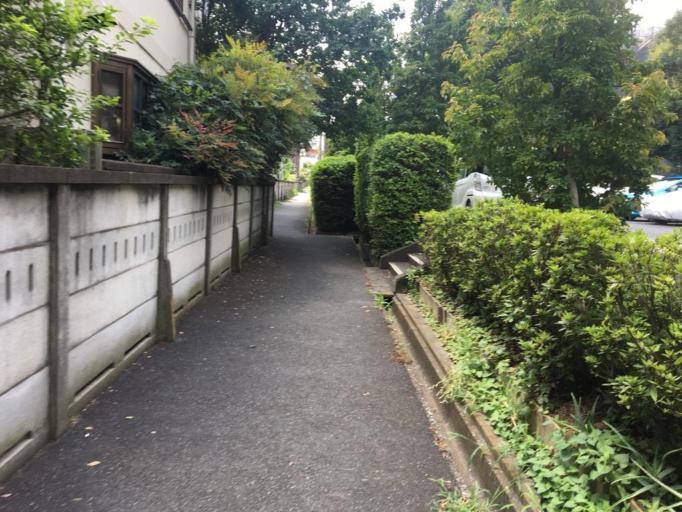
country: JP
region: Saitama
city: Wako
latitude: 35.7865
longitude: 139.6080
